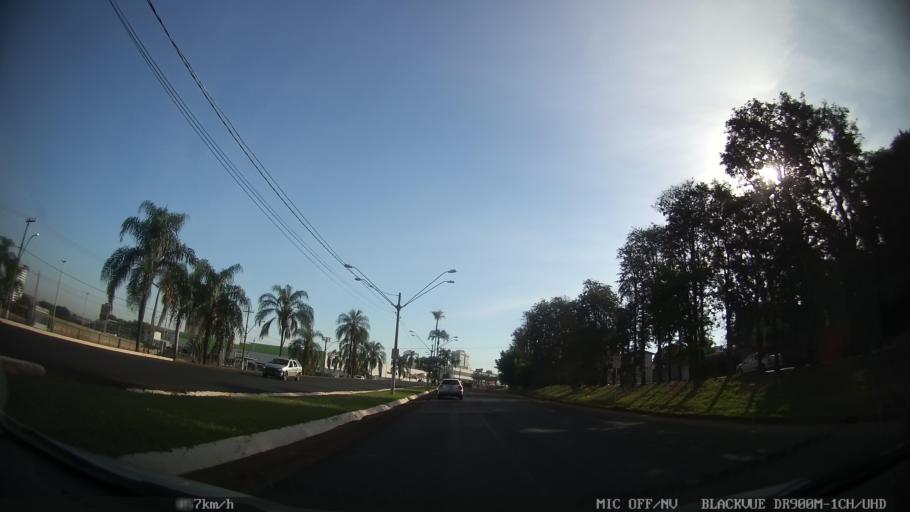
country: BR
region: Sao Paulo
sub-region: Ribeirao Preto
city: Ribeirao Preto
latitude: -21.2162
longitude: -47.8149
